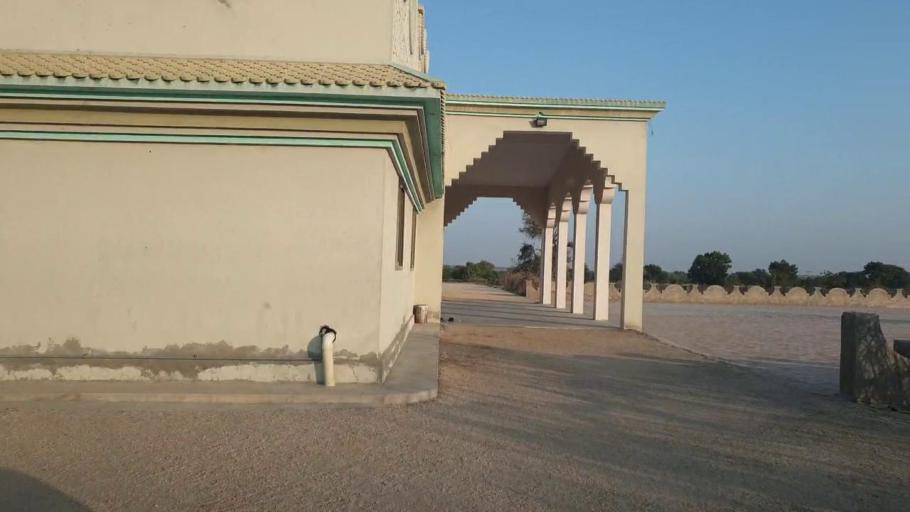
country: PK
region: Sindh
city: Chor
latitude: 25.5329
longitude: 69.8060
